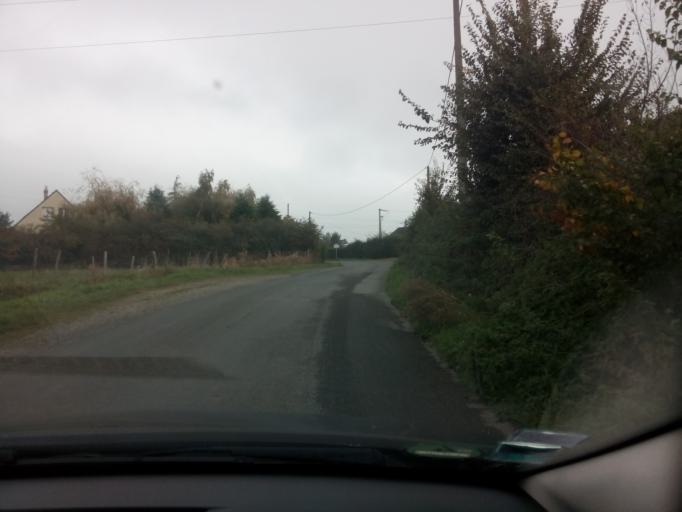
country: FR
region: Pays de la Loire
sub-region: Departement de Maine-et-Loire
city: Soulaire-et-Bourg
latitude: 47.5748
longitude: -0.5561
